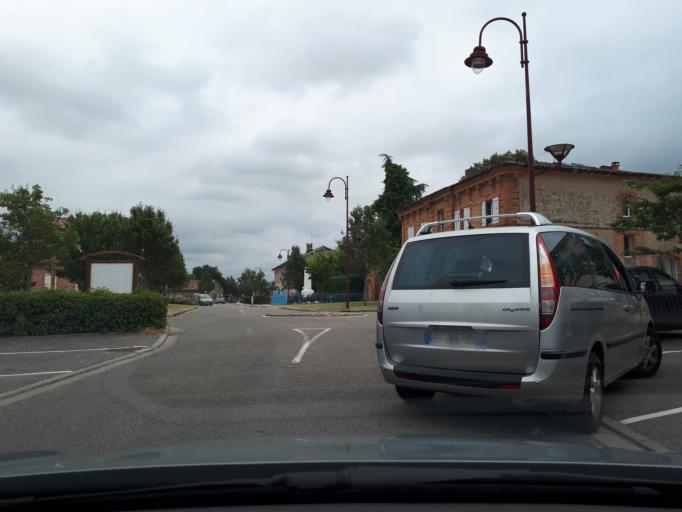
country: FR
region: Midi-Pyrenees
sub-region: Departement du Tarn-et-Garonne
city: Campsas
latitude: 43.8970
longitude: 1.3262
